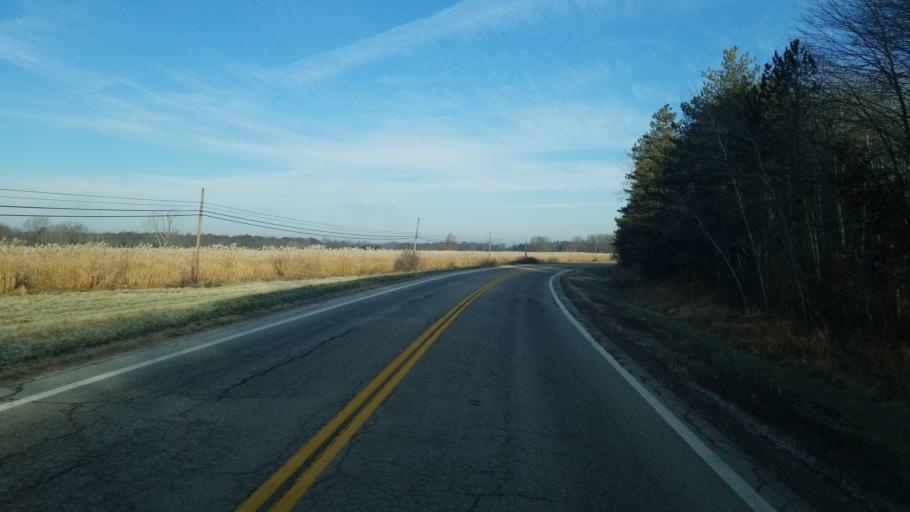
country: US
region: Ohio
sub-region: Ashtabula County
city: Jefferson
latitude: 41.7133
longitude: -80.6686
